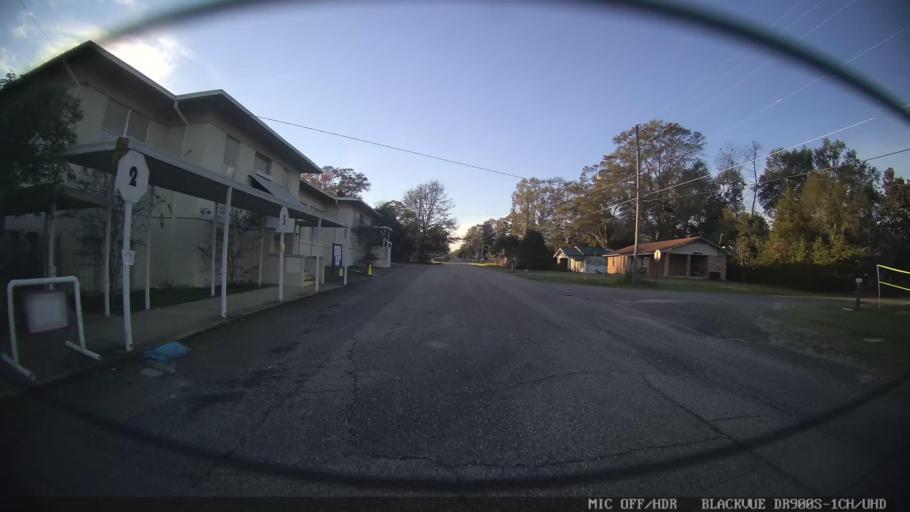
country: US
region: Mississippi
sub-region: Lamar County
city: Lumberton
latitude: 30.9987
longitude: -89.4519
